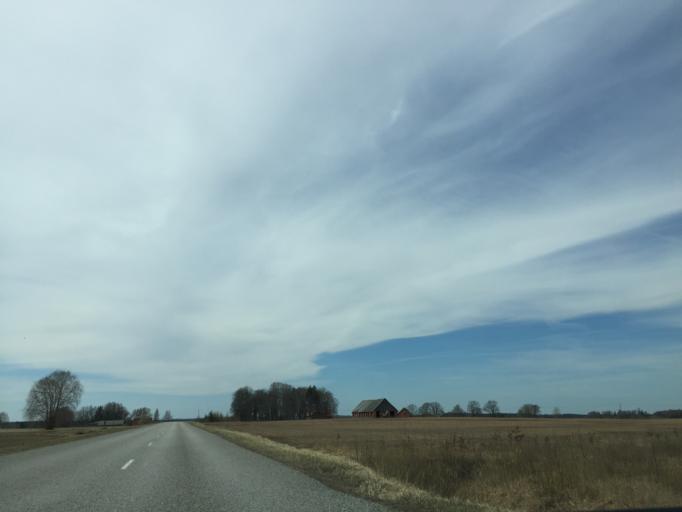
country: LV
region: Valkas Rajons
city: Valka
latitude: 57.7796
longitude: 25.9309
